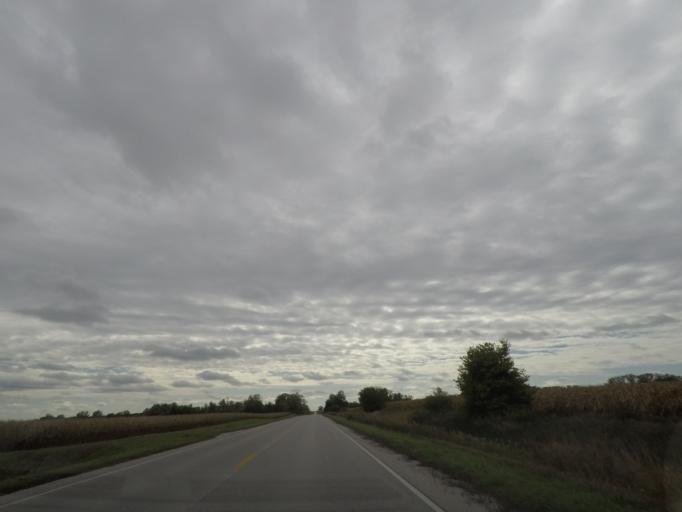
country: US
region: Iowa
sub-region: Story County
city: Huxley
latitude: 41.8734
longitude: -93.5315
